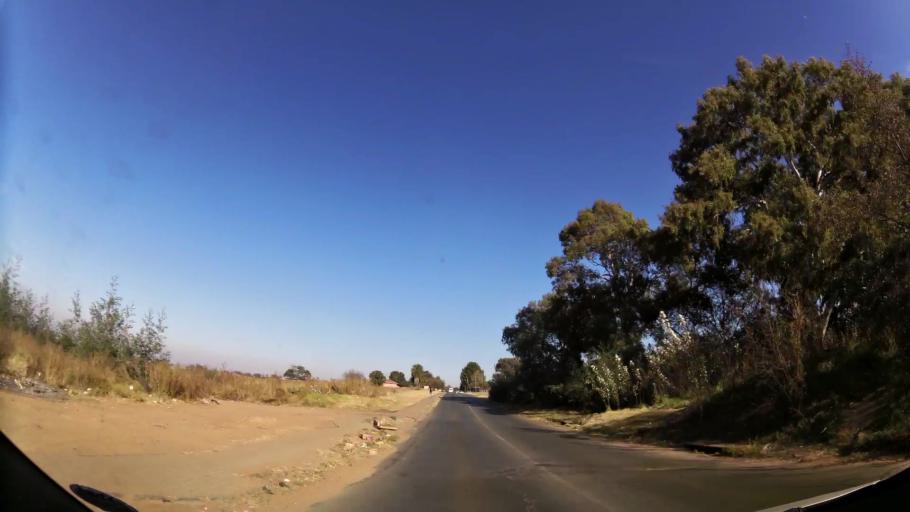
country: ZA
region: Gauteng
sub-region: City of Johannesburg Metropolitan Municipality
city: Roodepoort
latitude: -26.1509
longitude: 27.8389
